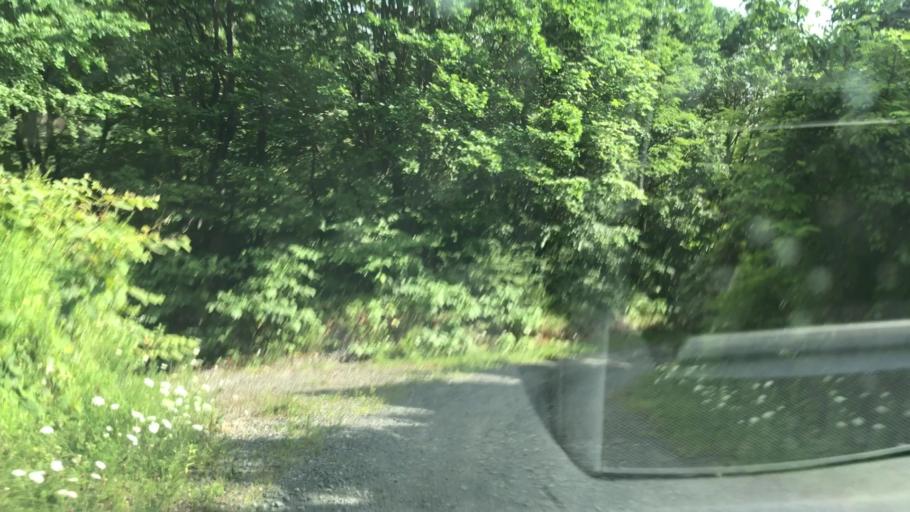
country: JP
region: Hokkaido
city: Shizunai-furukawacho
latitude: 42.7980
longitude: 142.3977
